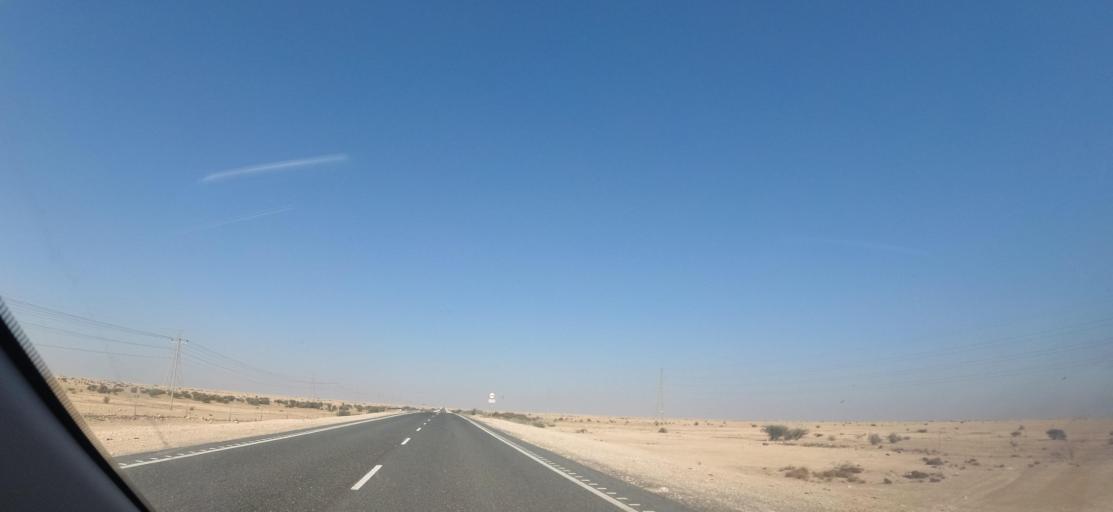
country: QA
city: Al Jumayliyah
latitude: 25.6708
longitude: 51.1281
